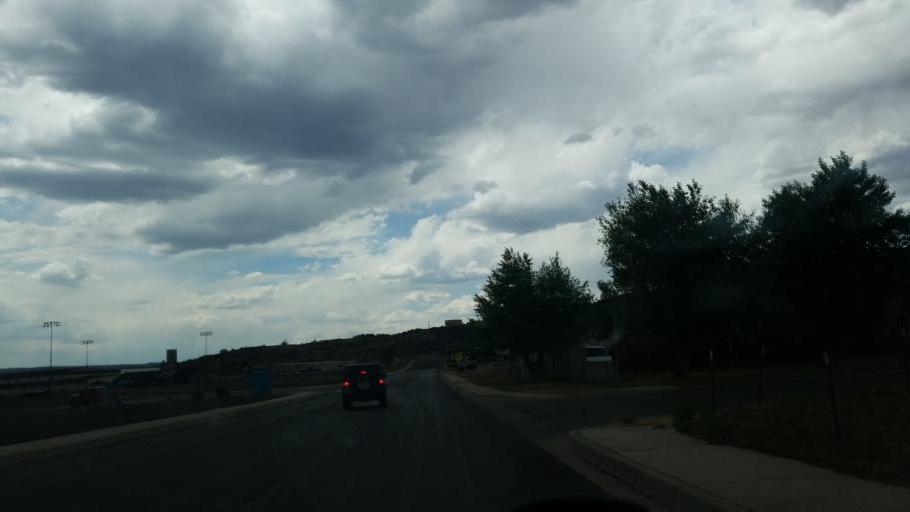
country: US
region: New Mexico
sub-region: Cibola County
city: Grants
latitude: 35.1611
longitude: -107.8421
